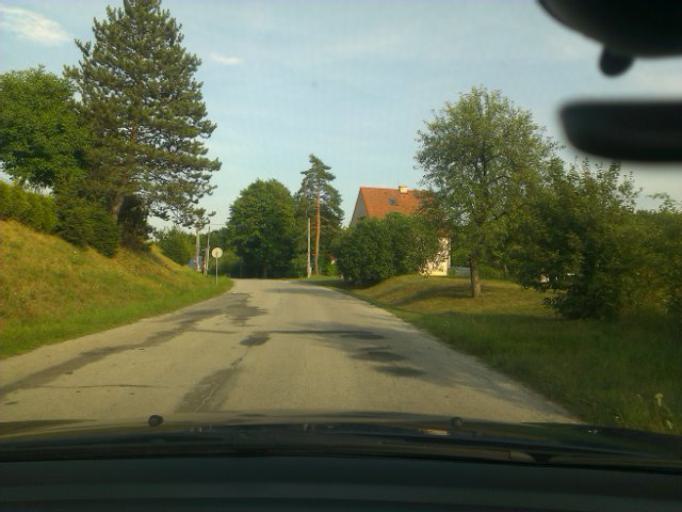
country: SK
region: Trenciansky
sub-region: Okres Myjava
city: Myjava
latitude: 48.7771
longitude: 17.5774
